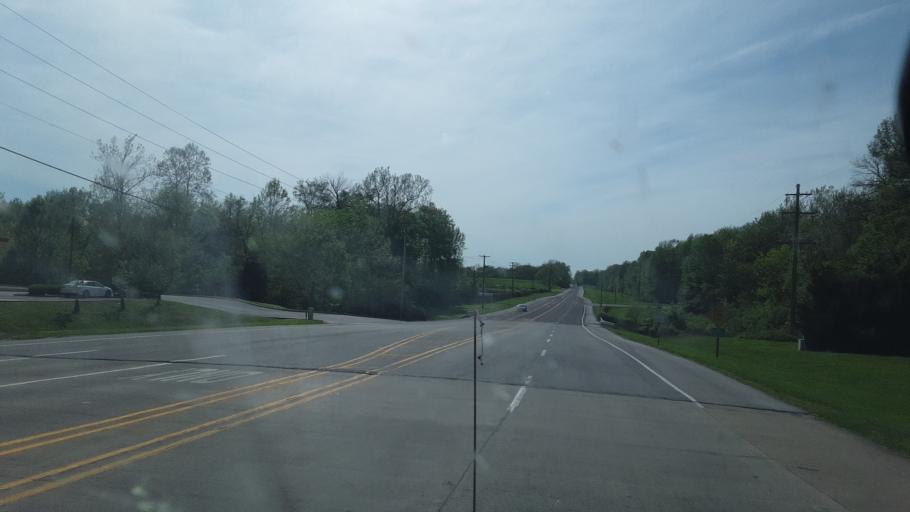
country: US
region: Illinois
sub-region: Jackson County
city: Carbondale
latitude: 37.7004
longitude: -89.2191
